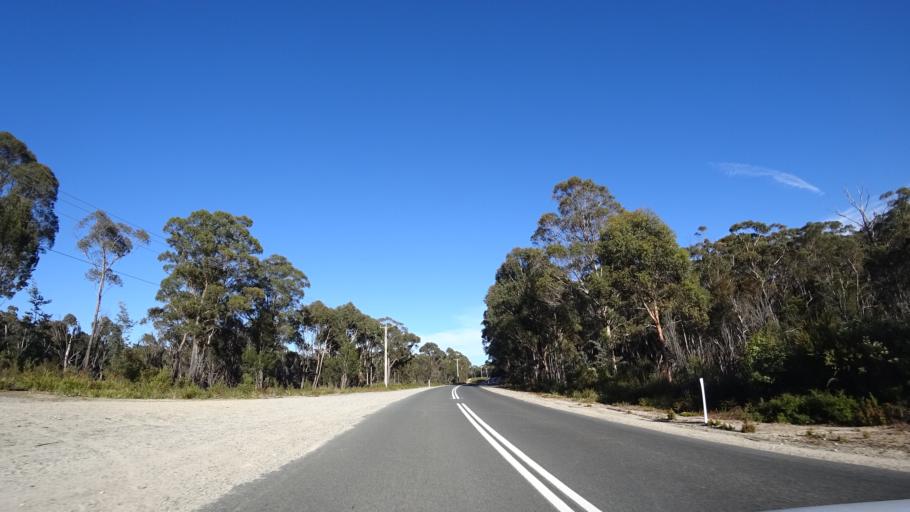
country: AU
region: Tasmania
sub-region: Break O'Day
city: St Helens
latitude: -41.2846
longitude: 148.1589
